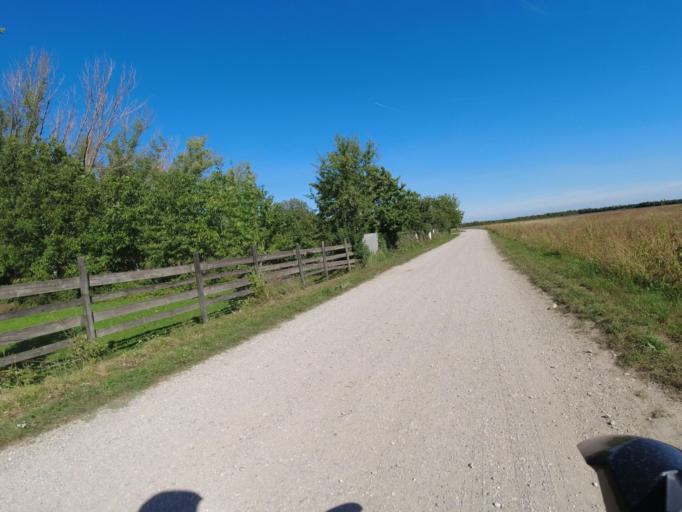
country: AT
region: Lower Austria
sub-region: Politischer Bezirk Modling
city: Guntramsdorf
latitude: 48.0217
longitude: 16.3186
